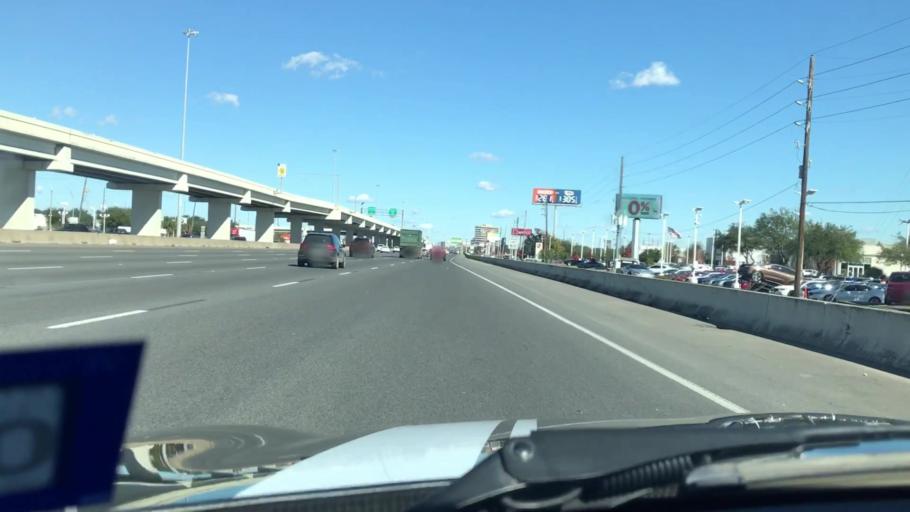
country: US
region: Texas
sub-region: Fort Bend County
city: Meadows Place
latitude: 29.6682
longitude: -95.5499
